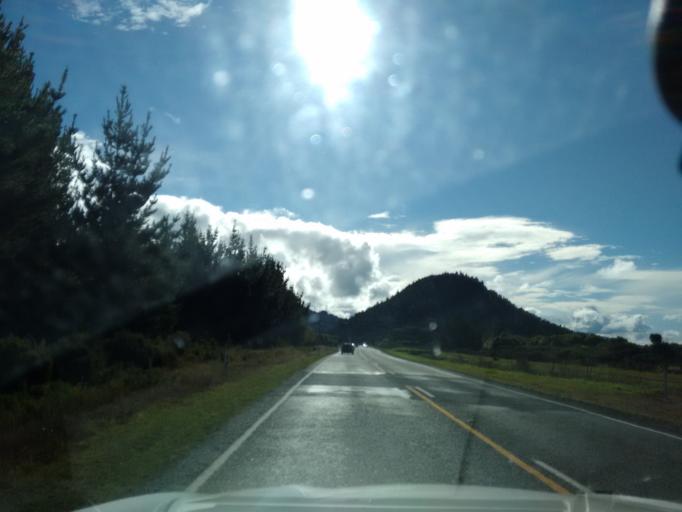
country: NZ
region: Waikato
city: Turangi
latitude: -38.9830
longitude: 175.7812
